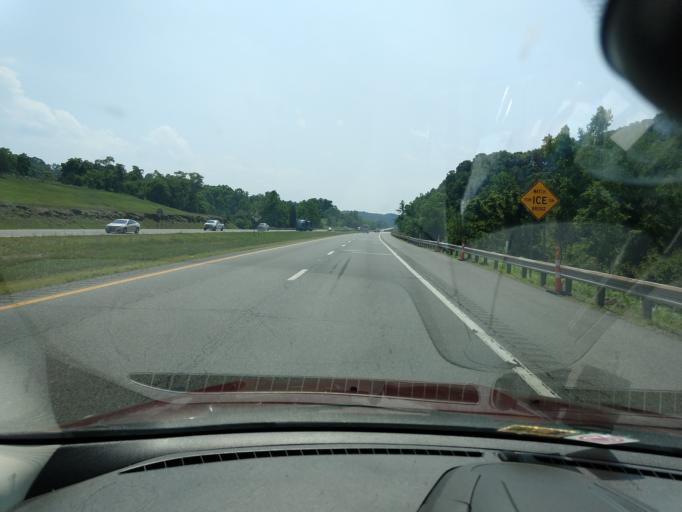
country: US
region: West Virginia
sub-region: Jackson County
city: Ripley
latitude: 38.7351
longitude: -81.6652
